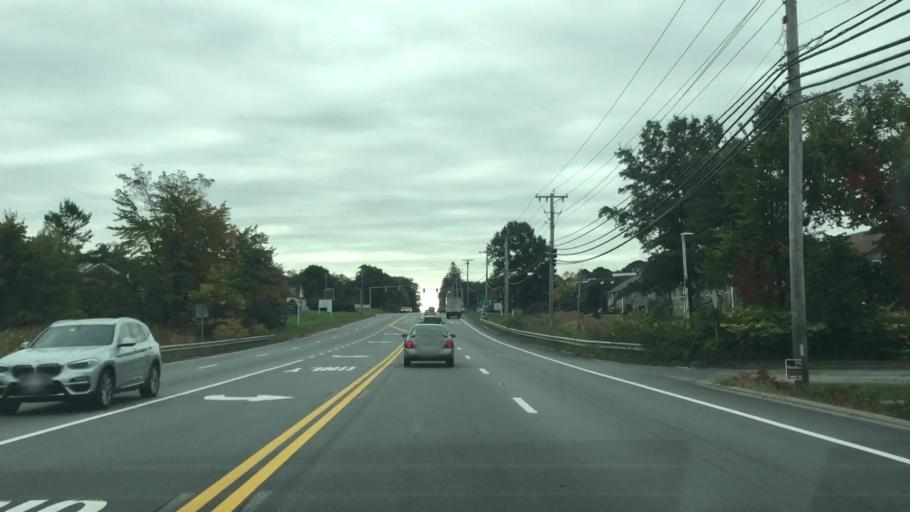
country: US
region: Massachusetts
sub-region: Essex County
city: Andover
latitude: 42.6602
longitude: -71.1081
